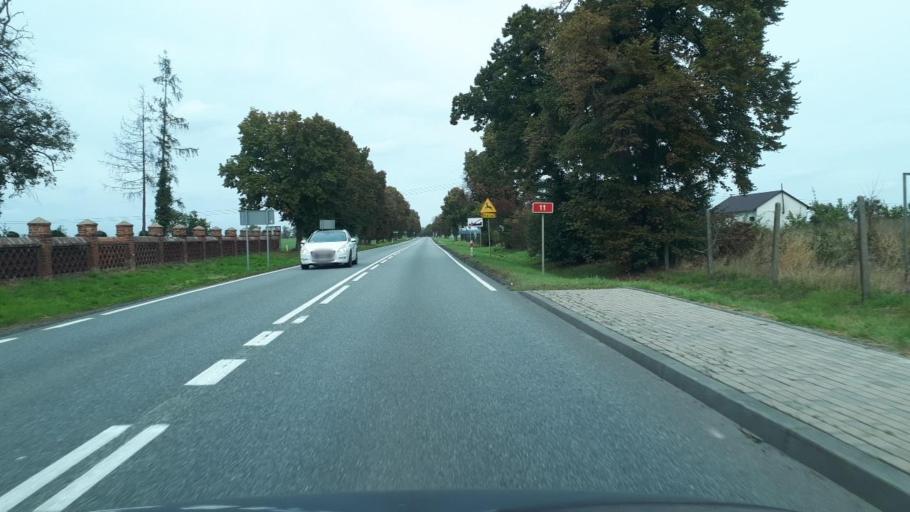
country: PL
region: Opole Voivodeship
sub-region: Powiat kluczborski
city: Kluczbork
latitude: 51.0302
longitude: 18.1924
